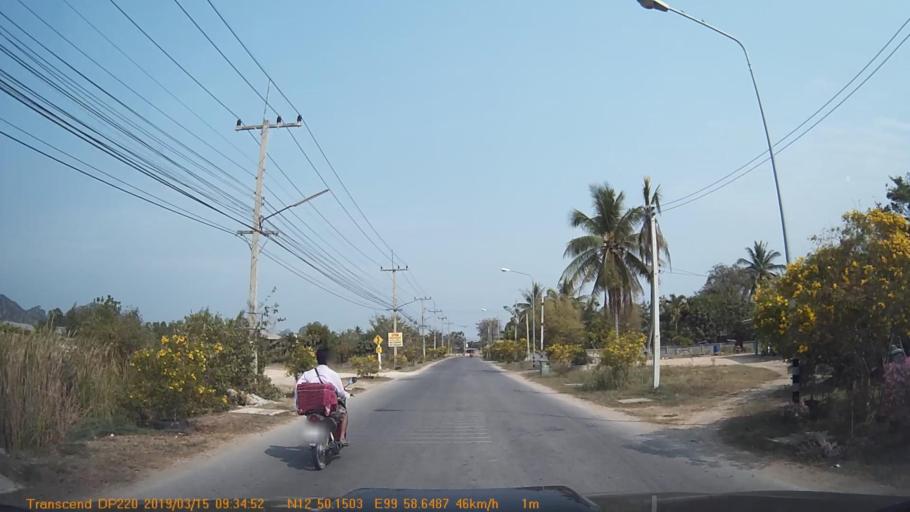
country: TH
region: Phetchaburi
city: Cha-am
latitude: 12.8360
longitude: 99.9774
